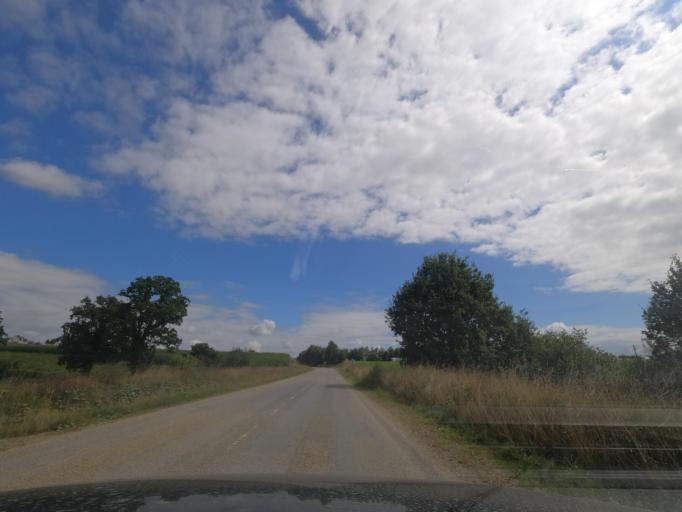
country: FR
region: Pays de la Loire
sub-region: Departement de la Mayenne
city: Fougerolles-du-Plessis
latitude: 48.4762
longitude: -0.9864
